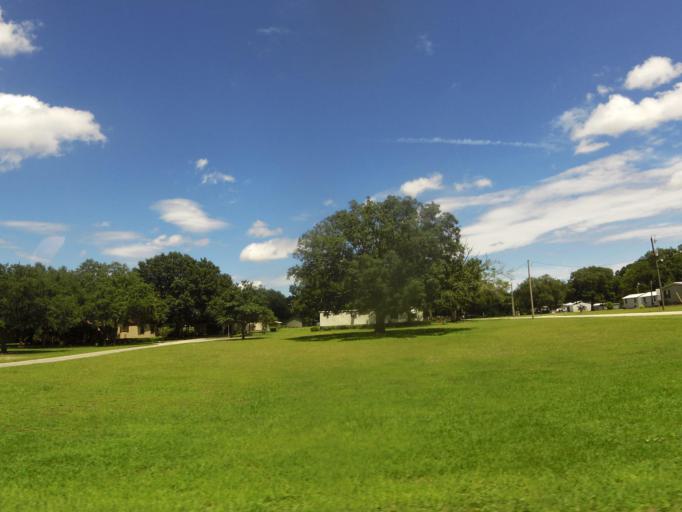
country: US
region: Georgia
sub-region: Camden County
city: St. Marys
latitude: 30.6664
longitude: -81.5412
